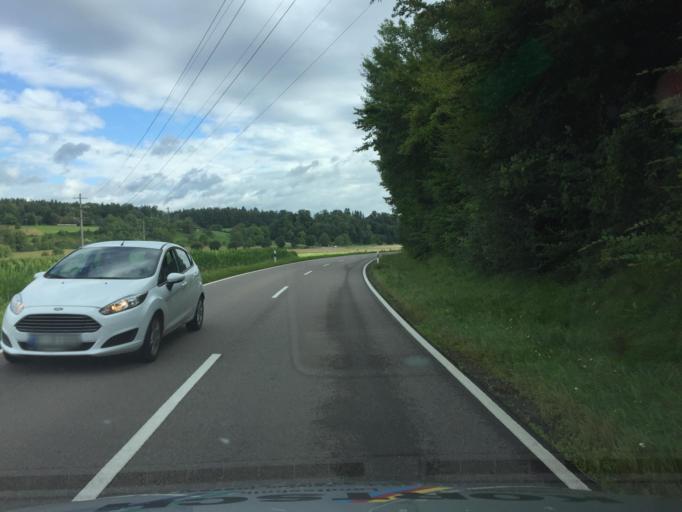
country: DE
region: Baden-Wuerttemberg
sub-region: Freiburg Region
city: Dettighofen
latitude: 47.6282
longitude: 8.4402
